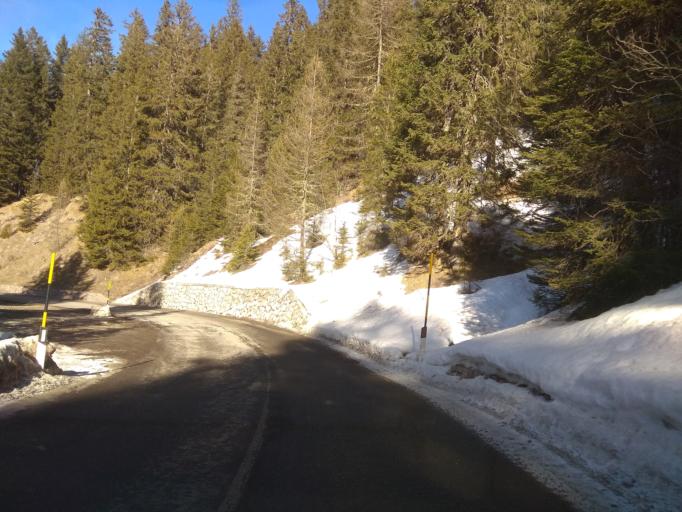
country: IT
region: Trentino-Alto Adige
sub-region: Bolzano
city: Nova Levante
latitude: 46.4393
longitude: 11.5895
